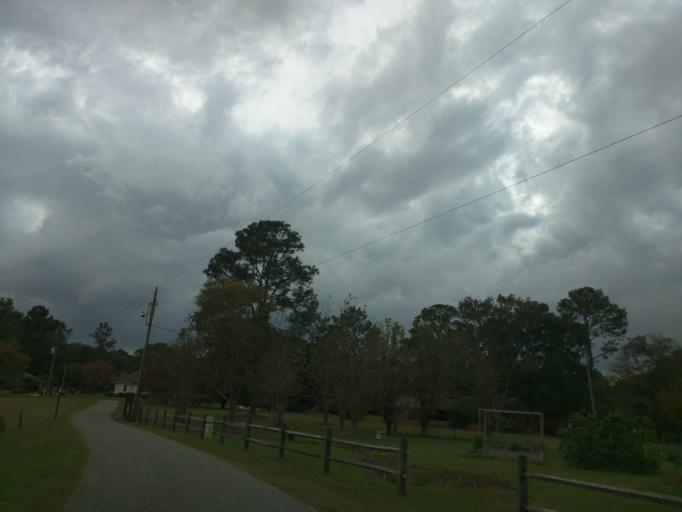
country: US
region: Florida
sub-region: Leon County
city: Tallahassee
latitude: 30.4815
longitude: -84.1898
